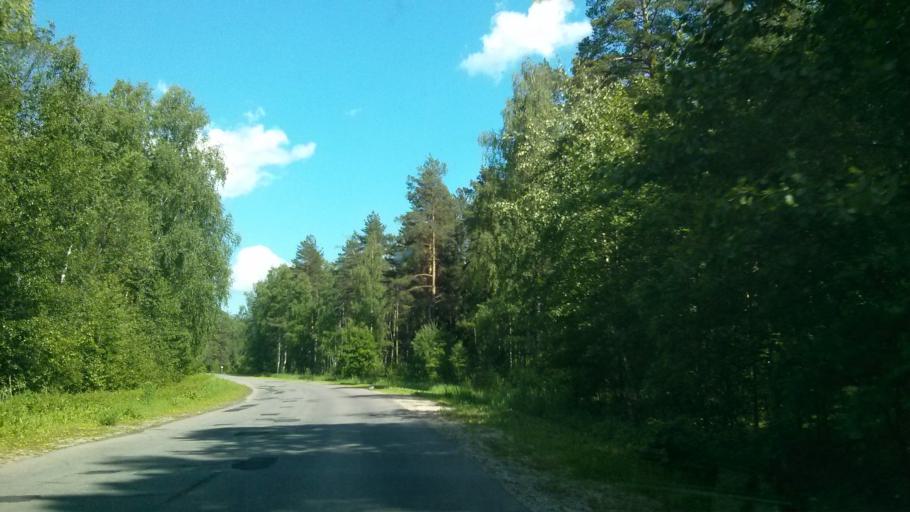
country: RU
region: Vladimir
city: Melenki
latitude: 55.3335
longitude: 41.6724
